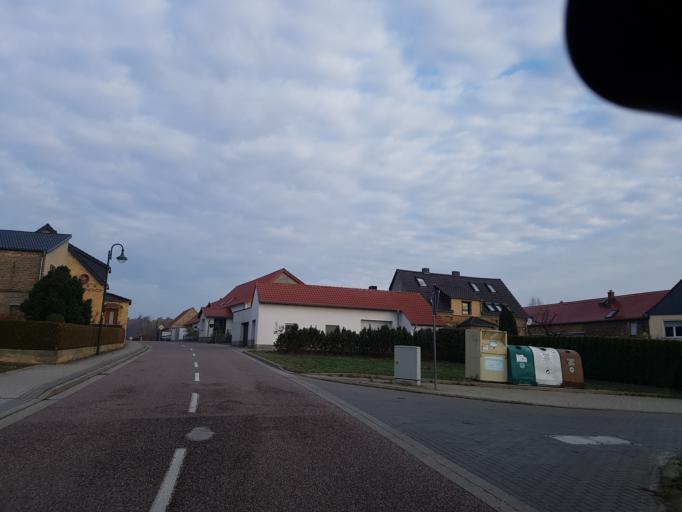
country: DE
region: Saxony-Anhalt
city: Kropstadt
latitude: 51.9372
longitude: 12.7571
